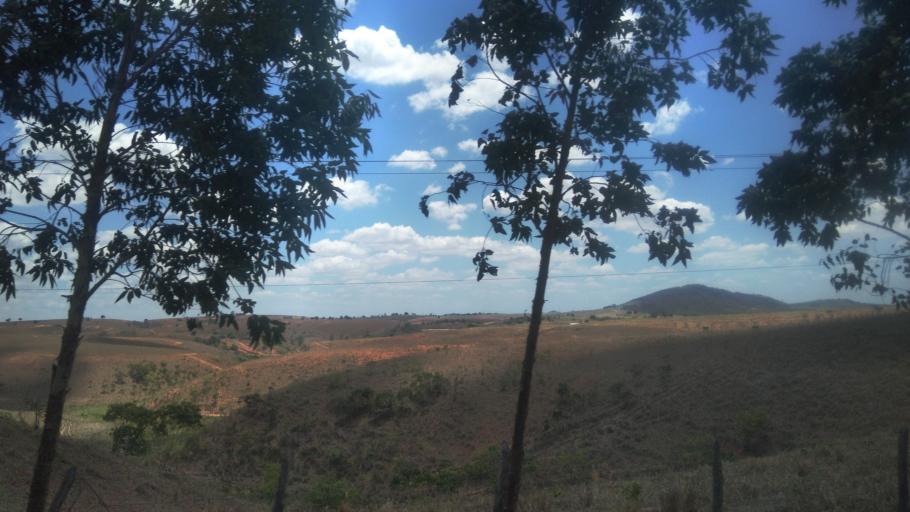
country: BR
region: Pernambuco
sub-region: Nazare Da Mata
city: Nazare da Mata
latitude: -7.7338
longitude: -35.2790
